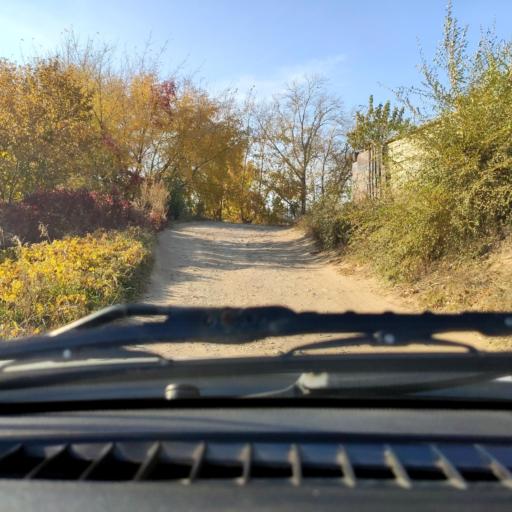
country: RU
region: Samara
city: Zhigulevsk
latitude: 53.4715
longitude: 49.5020
